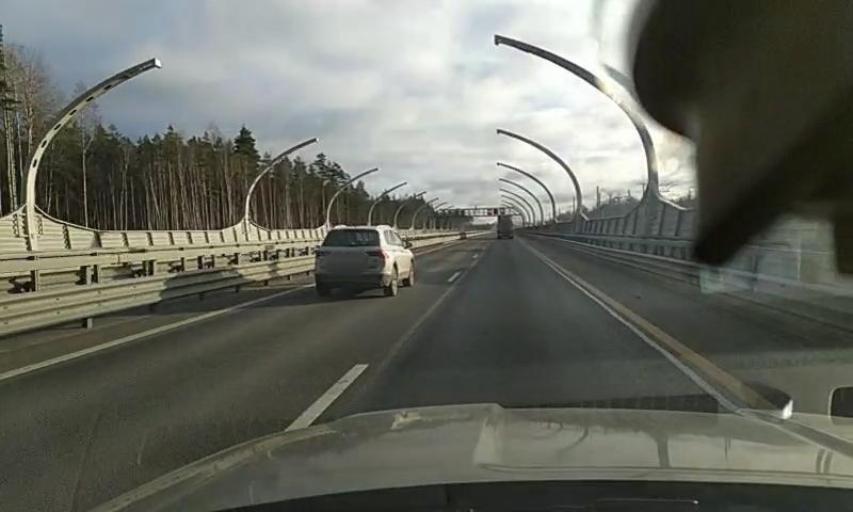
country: RU
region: St.-Petersburg
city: Beloostrov
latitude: 60.1416
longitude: 30.0305
